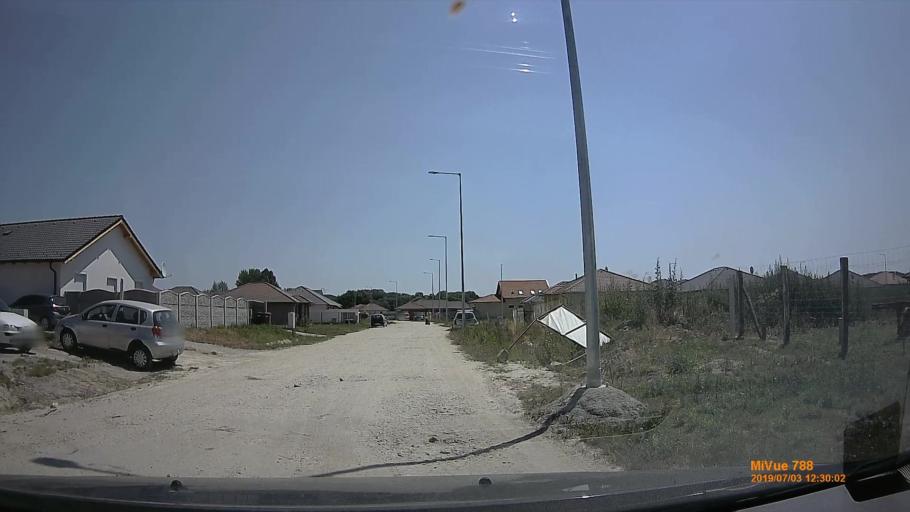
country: HU
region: Gyor-Moson-Sopron
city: Gyor
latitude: 47.7148
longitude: 17.6071
